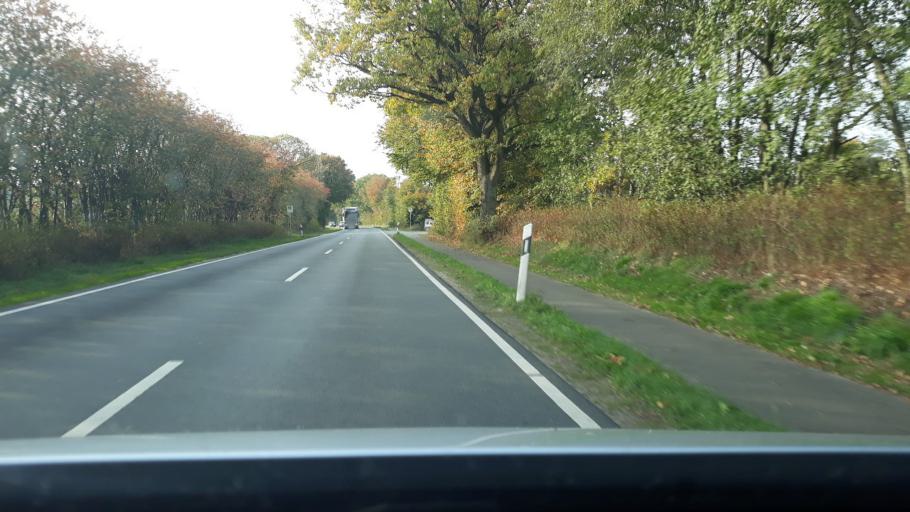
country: DE
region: Schleswig-Holstein
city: Owschlag
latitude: 54.3975
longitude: 9.5588
